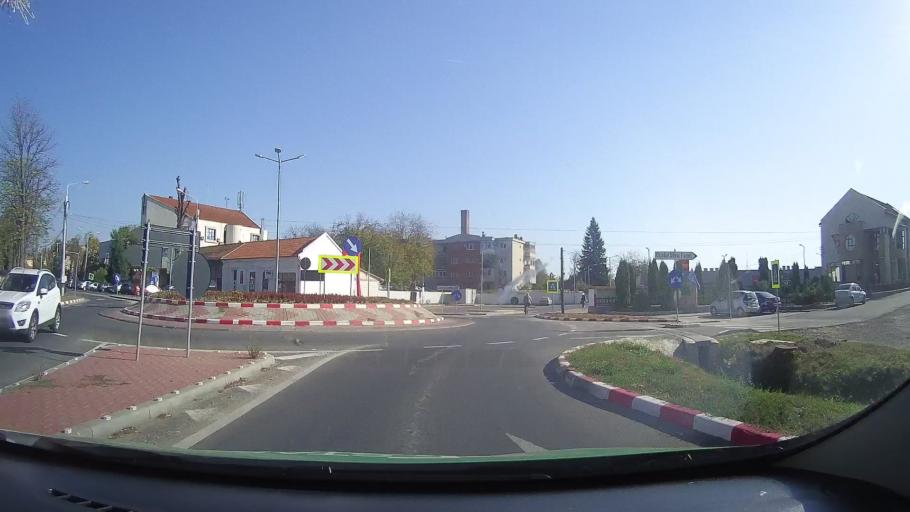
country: RO
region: Timis
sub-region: Comuna Faget
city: Faget
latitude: 45.8540
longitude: 22.1769
